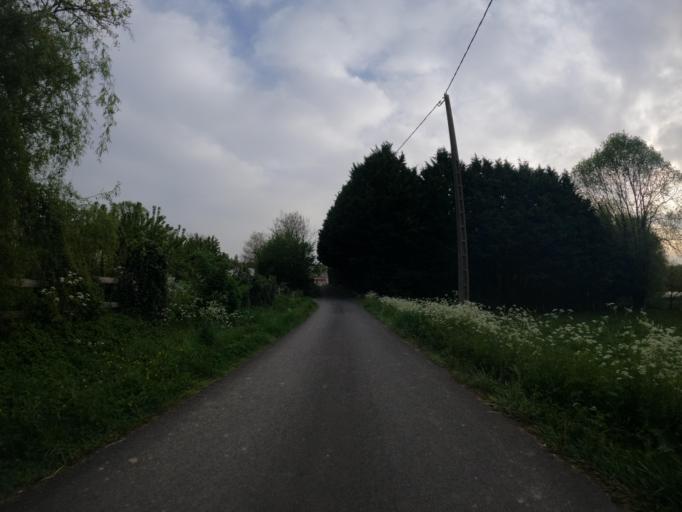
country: FR
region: Poitou-Charentes
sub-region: Departement des Deux-Sevres
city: La Chapelle-Saint-Laurent
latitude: 46.6967
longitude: -0.4898
